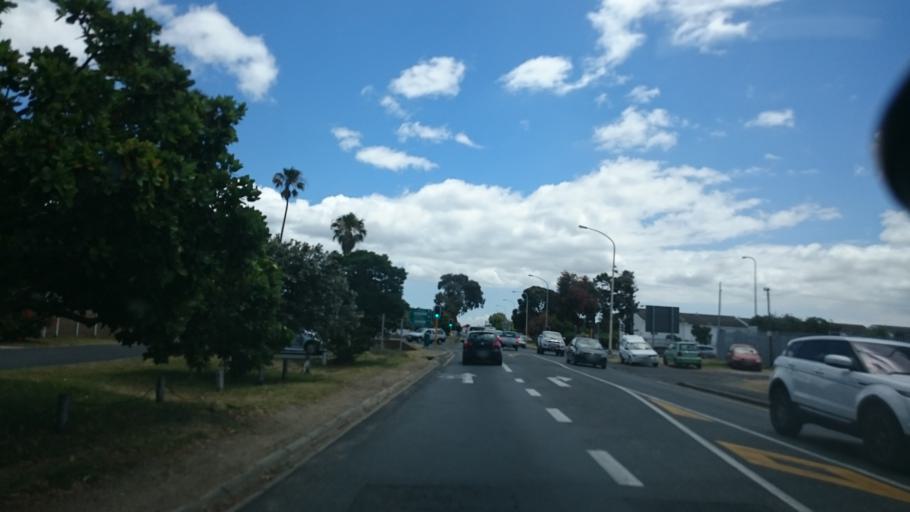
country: ZA
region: Western Cape
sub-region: City of Cape Town
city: Bergvliet
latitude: -34.0432
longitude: 18.4635
